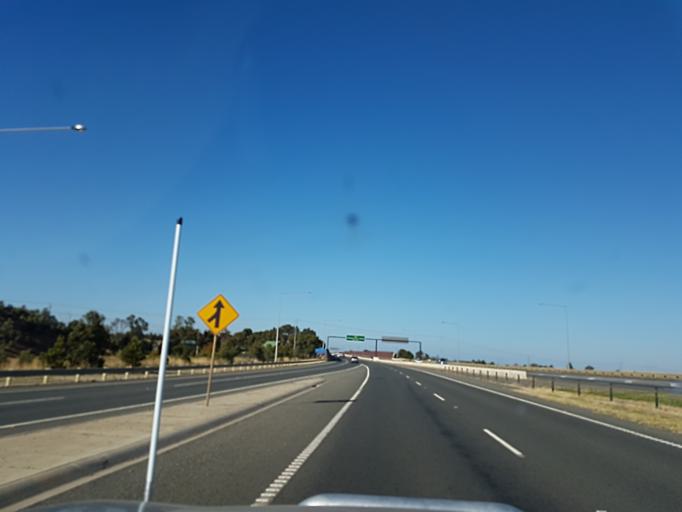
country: AU
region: Victoria
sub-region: Greater Geelong
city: Wandana Heights
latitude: -38.2157
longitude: 144.2903
